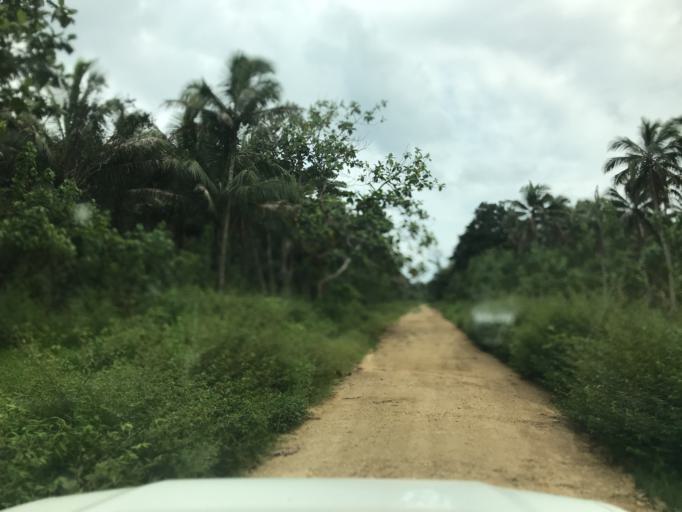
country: VU
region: Sanma
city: Port-Olry
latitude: -15.1865
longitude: 167.0225
